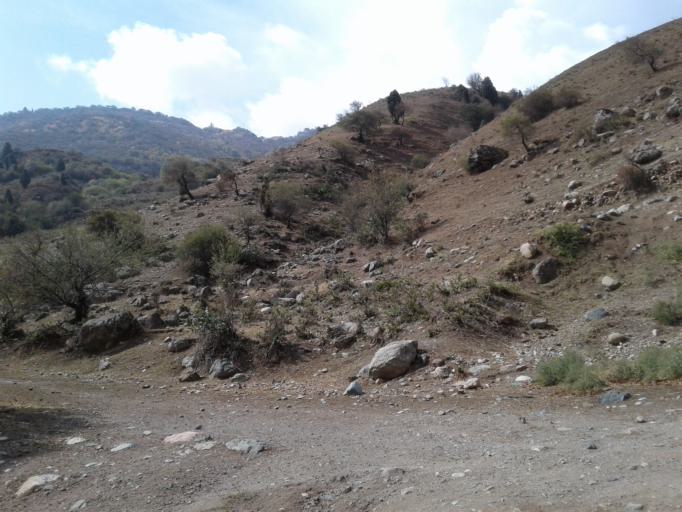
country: TJ
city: Shahrinav
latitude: 38.6993
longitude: 68.3683
